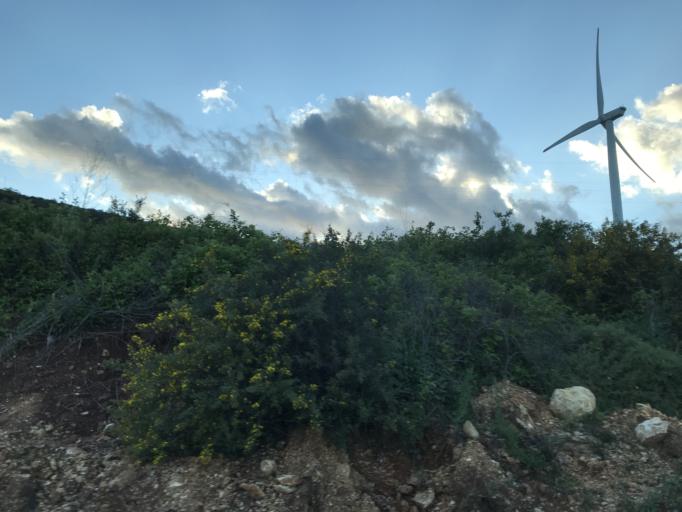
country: TR
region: Hatay
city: Buyukcat
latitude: 36.0997
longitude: 36.0424
